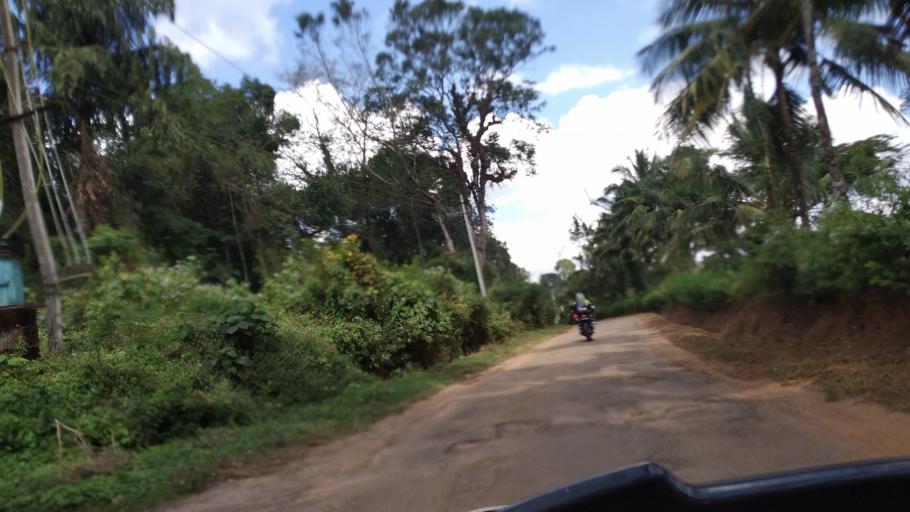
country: IN
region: Karnataka
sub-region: Kodagu
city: Ponnampet
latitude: 12.0265
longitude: 75.8935
